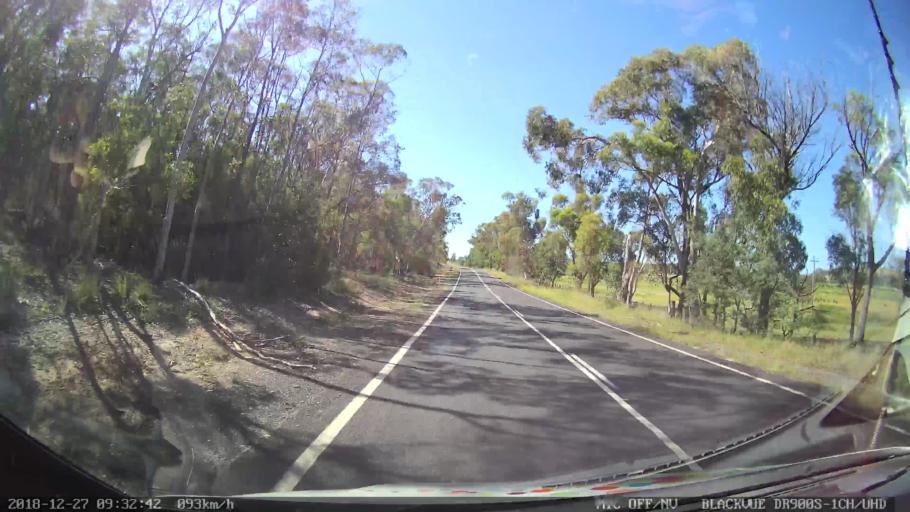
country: AU
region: New South Wales
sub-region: Lithgow
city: Portland
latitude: -33.2108
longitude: 150.0170
